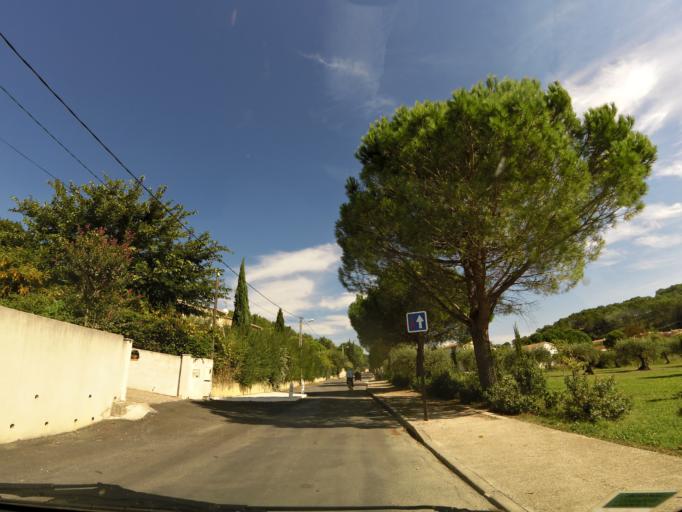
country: FR
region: Languedoc-Roussillon
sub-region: Departement du Gard
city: Nages-et-Solorgues
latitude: 43.7884
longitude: 4.2360
